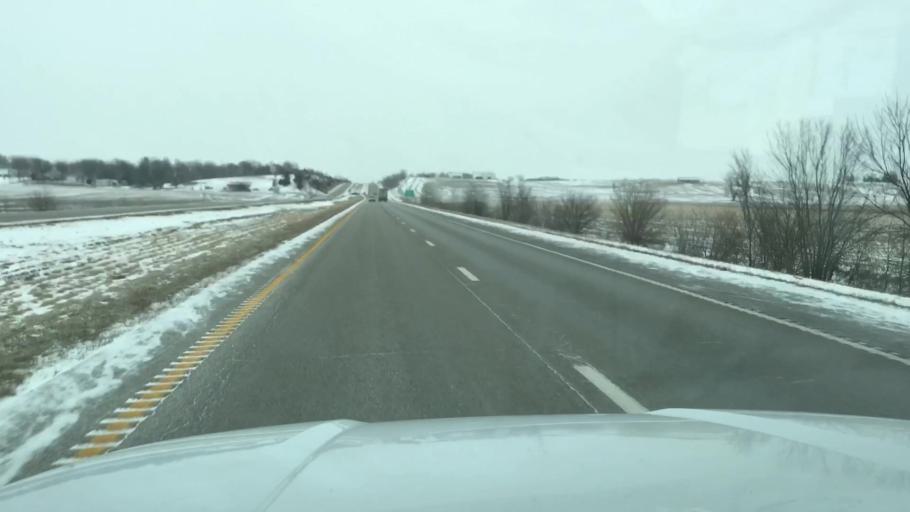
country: US
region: Missouri
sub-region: Buchanan County
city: Saint Joseph
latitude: 39.7478
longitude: -94.7190
